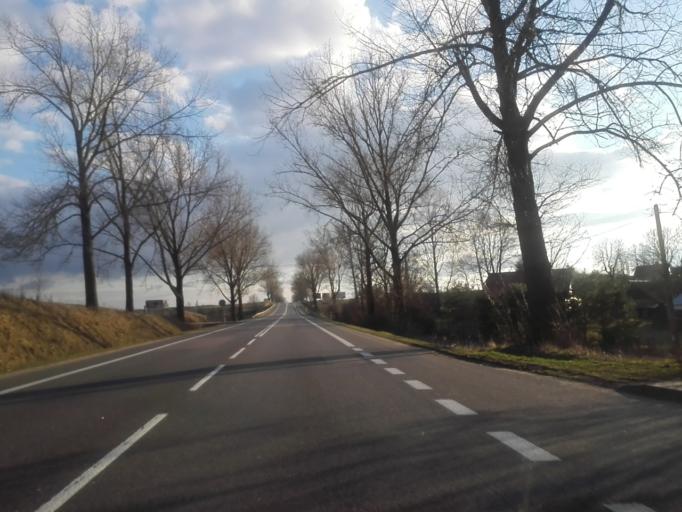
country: PL
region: Podlasie
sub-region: Suwalki
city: Suwalki
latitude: 54.1393
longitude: 22.9591
